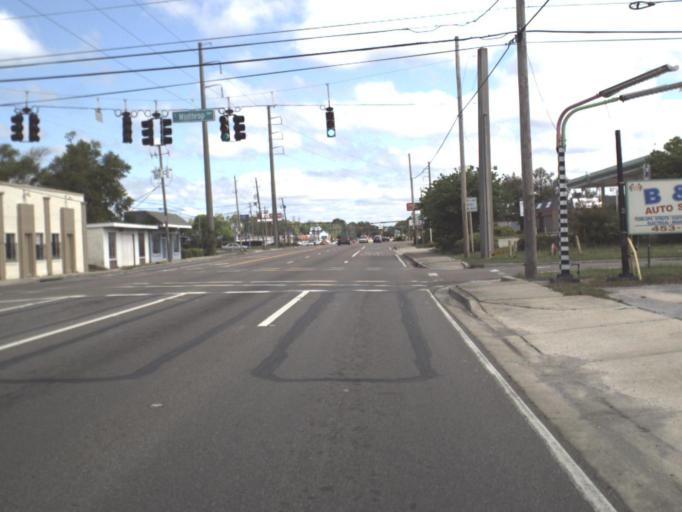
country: US
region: Florida
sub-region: Escambia County
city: Warrington
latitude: 30.3852
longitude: -87.2780
